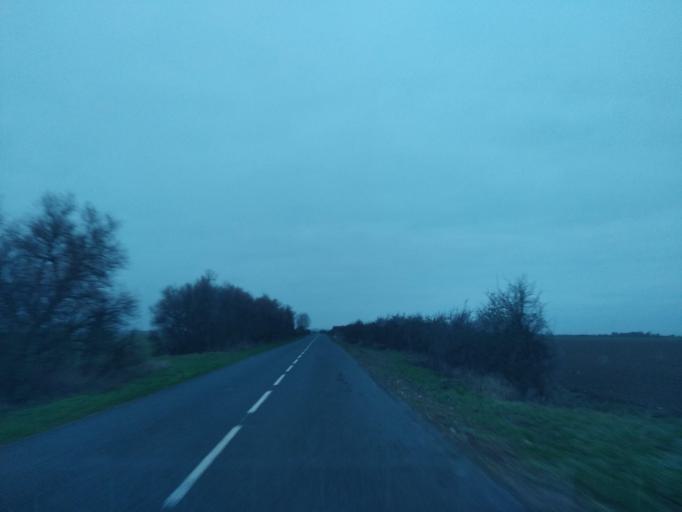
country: FR
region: Pays de la Loire
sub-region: Departement de la Vendee
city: Triaize
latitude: 46.3747
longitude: -1.2593
